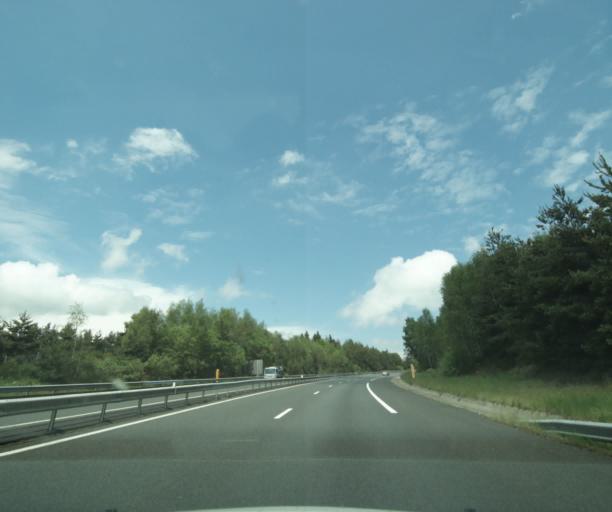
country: FR
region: Auvergne
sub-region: Departement du Cantal
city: Saint-Flour
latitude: 45.0849
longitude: 3.1179
